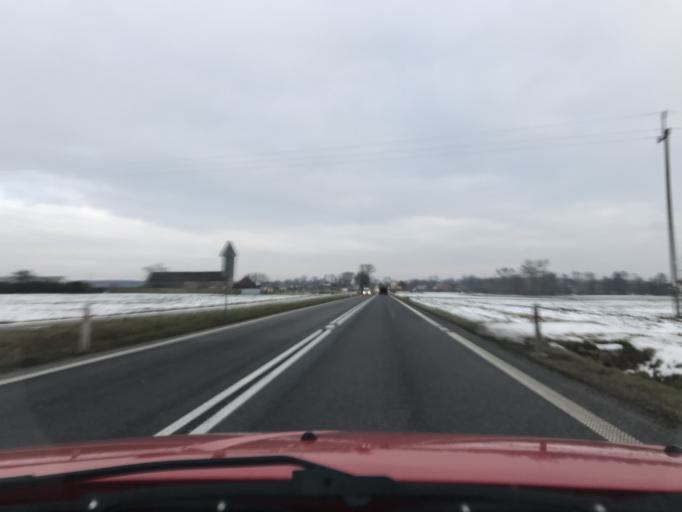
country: PL
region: Greater Poland Voivodeship
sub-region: Powiat pleszewski
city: Pleszew
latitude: 51.8880
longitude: 17.8491
